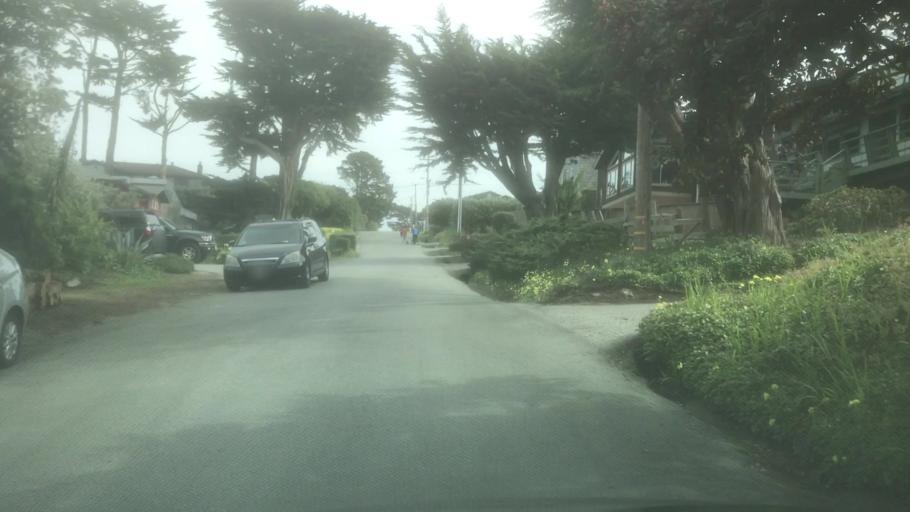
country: US
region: California
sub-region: San Mateo County
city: Montara
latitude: 37.5406
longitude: -122.5138
